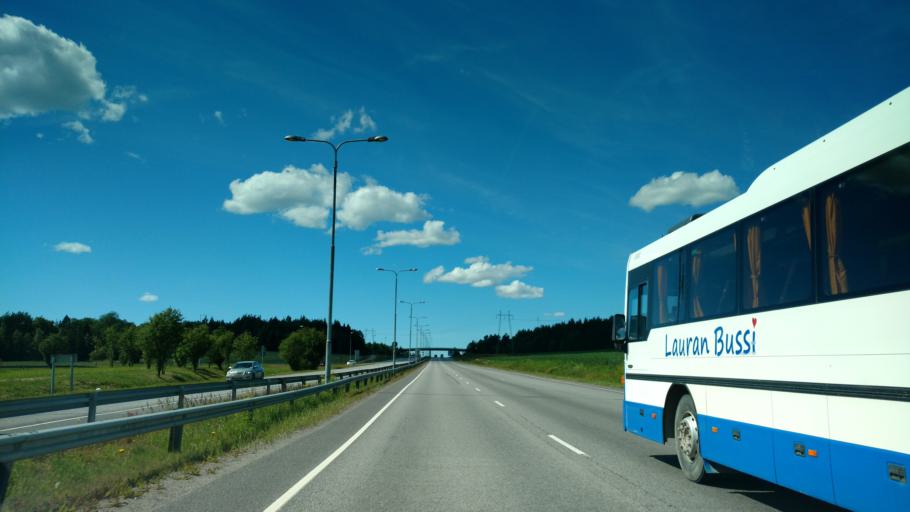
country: FI
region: Varsinais-Suomi
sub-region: Turku
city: Kaarina
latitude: 60.4732
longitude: 22.3567
